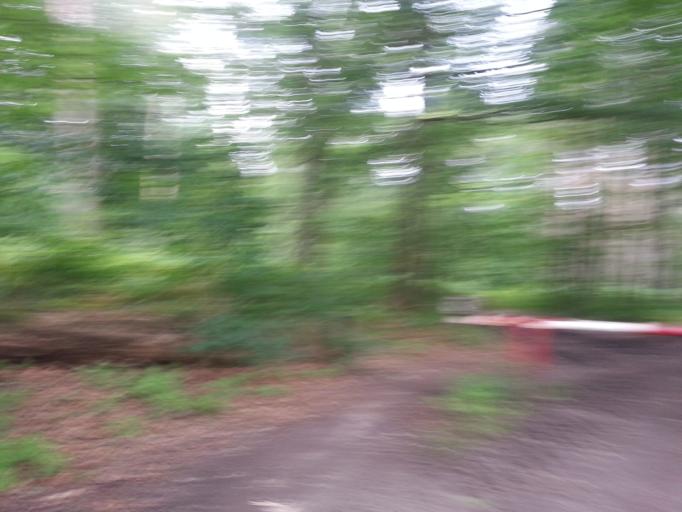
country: DE
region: North Rhine-Westphalia
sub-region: Regierungsbezirk Munster
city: Haltern
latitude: 51.7088
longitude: 7.2216
